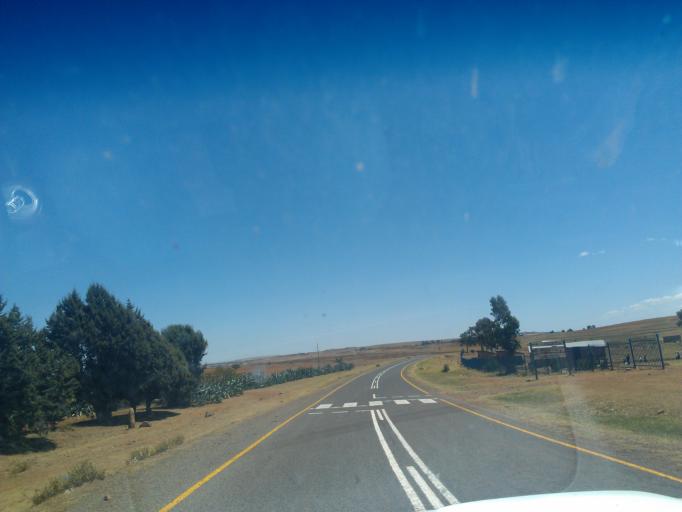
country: LS
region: Berea
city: Teyateyaneng
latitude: -29.2596
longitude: 27.7226
